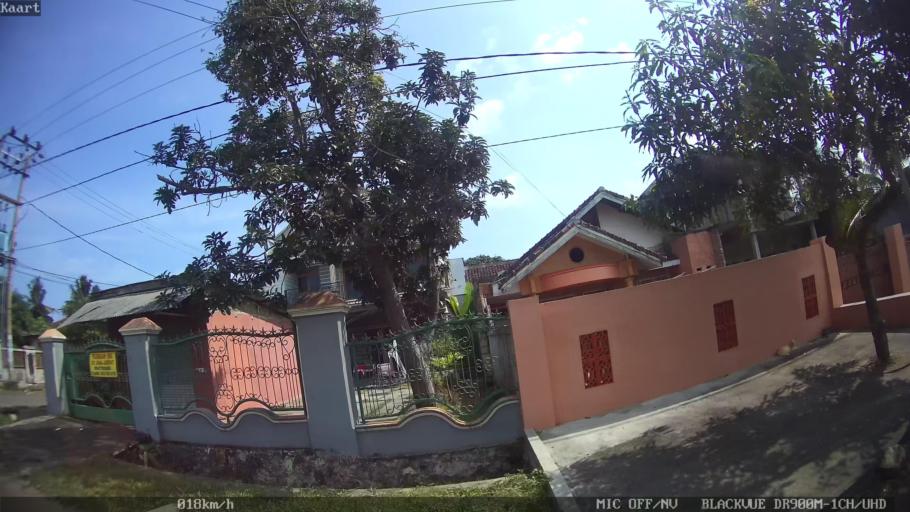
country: ID
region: Lampung
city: Kedaton
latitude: -5.4005
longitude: 105.2346
